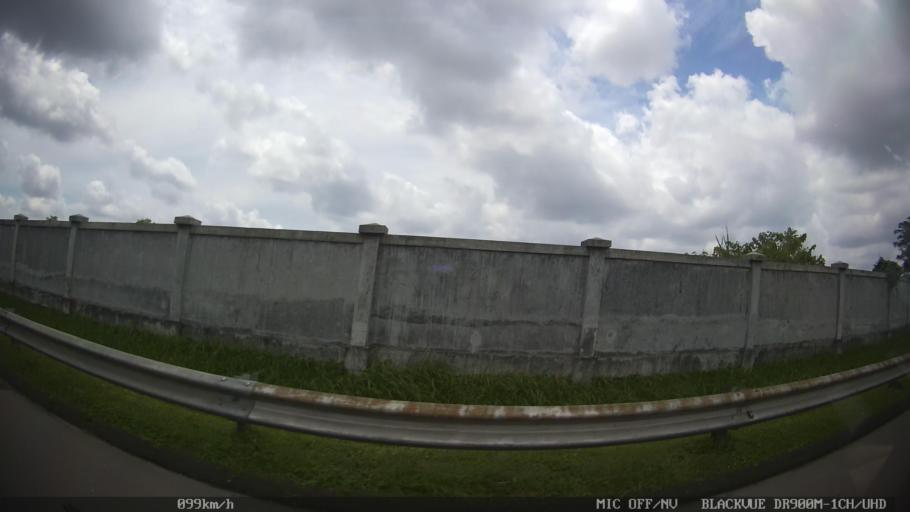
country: ID
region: North Sumatra
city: Medan
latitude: 3.6343
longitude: 98.7120
